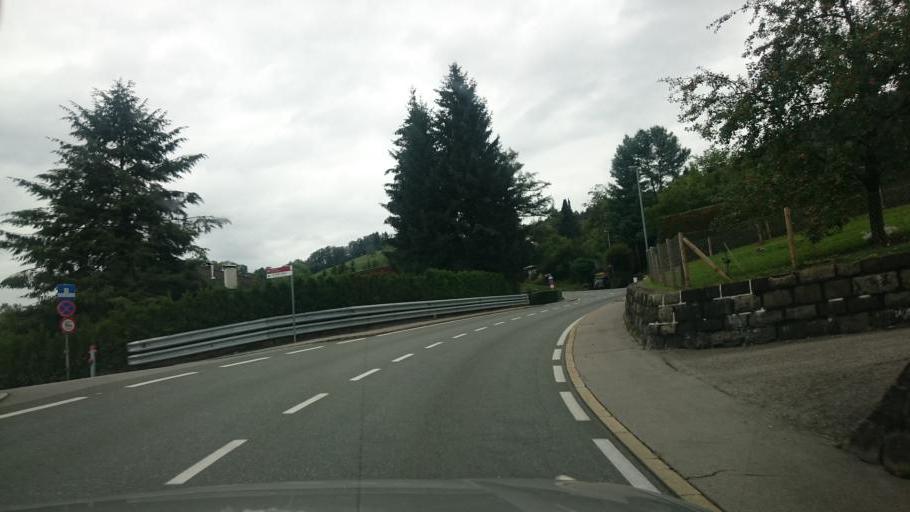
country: AT
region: Vorarlberg
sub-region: Politischer Bezirk Dornbirn
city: Dornbirn
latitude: 47.4108
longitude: 9.7554
